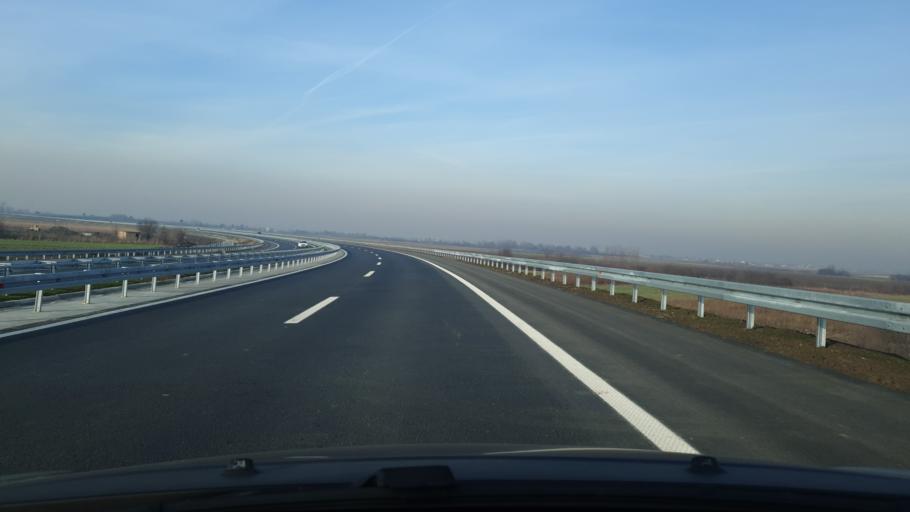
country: RS
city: Boljevci
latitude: 44.7210
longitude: 20.2579
